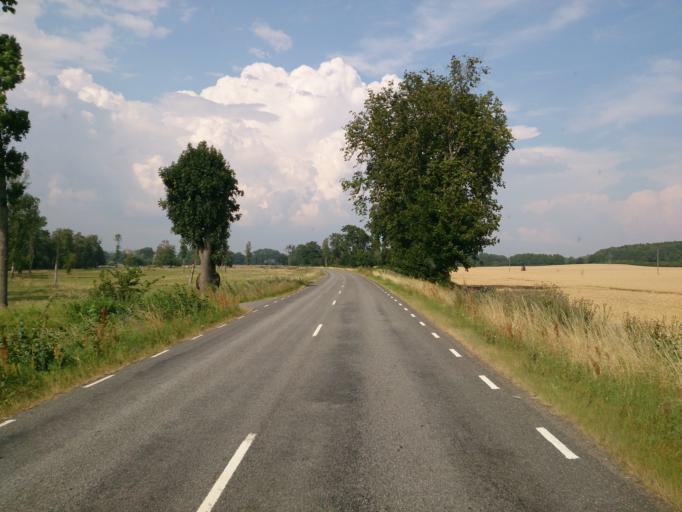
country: SE
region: Skane
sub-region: Kristianstads Kommun
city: Fjalkinge
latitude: 56.0738
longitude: 14.3455
